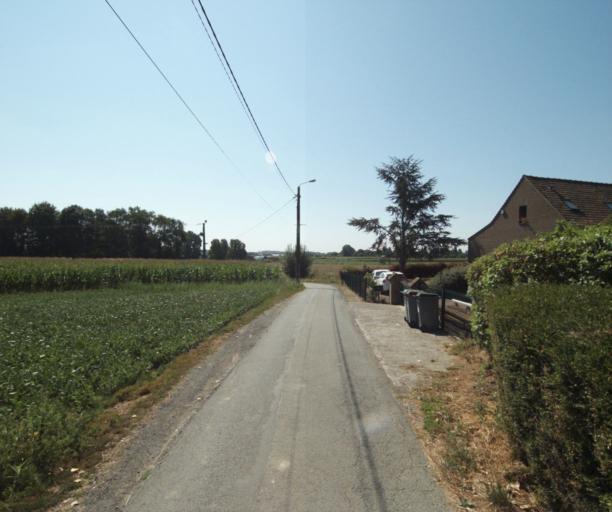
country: FR
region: Nord-Pas-de-Calais
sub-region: Departement du Nord
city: Bousbecque
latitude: 50.7572
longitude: 3.0969
